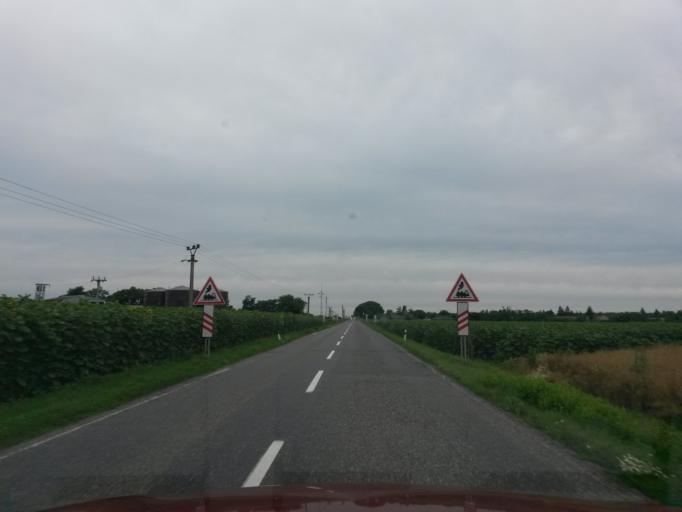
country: SK
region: Nitriansky
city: Levice
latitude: 48.1598
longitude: 18.5571
